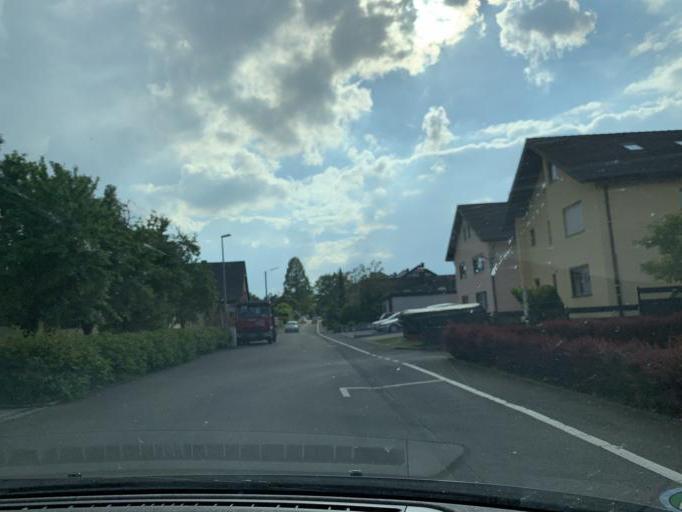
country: DE
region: North Rhine-Westphalia
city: Bruhl
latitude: 50.7961
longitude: 6.8917
